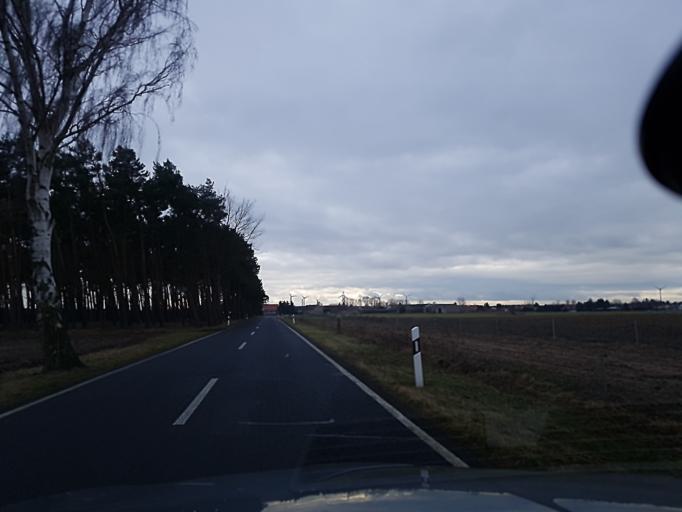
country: DE
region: Brandenburg
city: Schilda
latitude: 51.5526
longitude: 13.3373
